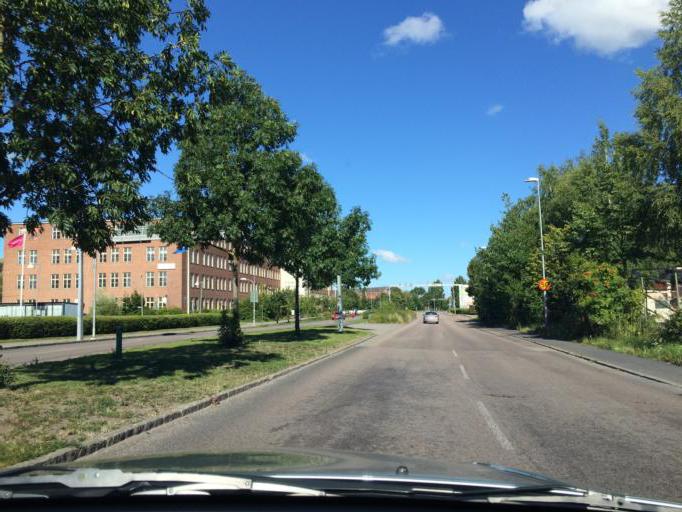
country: SE
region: Vaestmanland
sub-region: Vasteras
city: Vasteras
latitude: 59.6099
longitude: 16.5680
